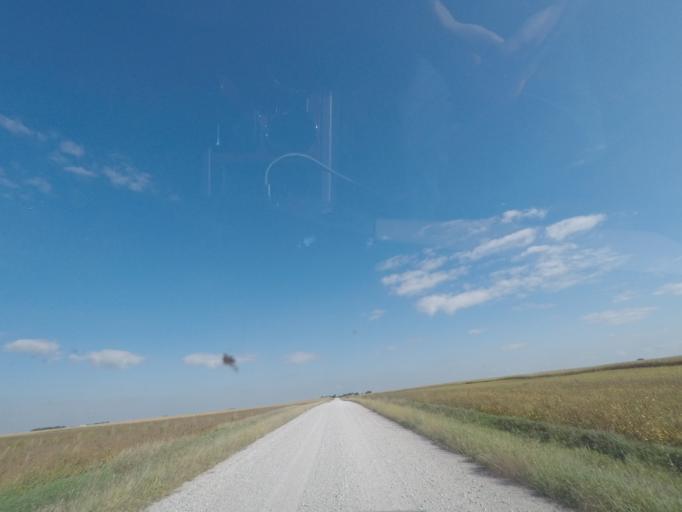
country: US
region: Iowa
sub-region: Story County
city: Nevada
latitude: 42.0463
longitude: -93.4252
